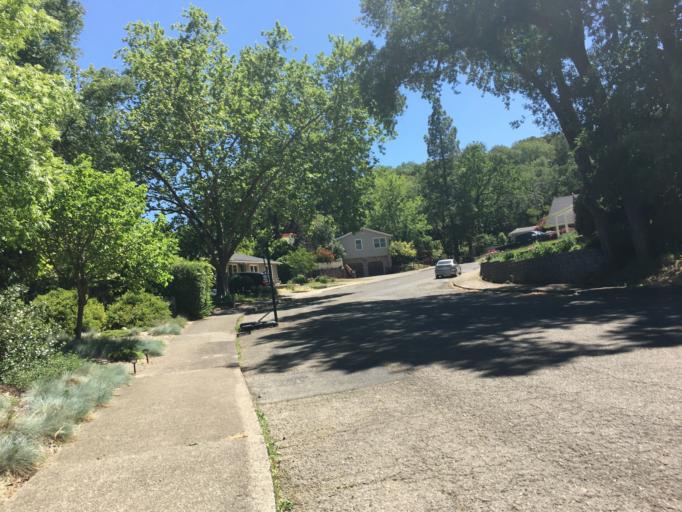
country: US
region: California
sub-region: Mendocino County
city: Ukiah
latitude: 39.1401
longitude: -123.2160
